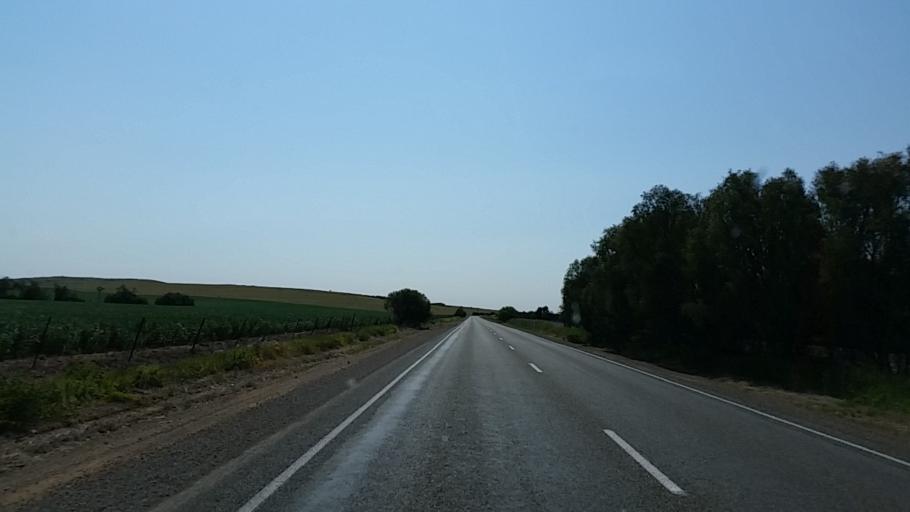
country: AU
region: South Australia
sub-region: Port Pirie City and Dists
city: Crystal Brook
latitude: -33.2470
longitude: 138.3694
